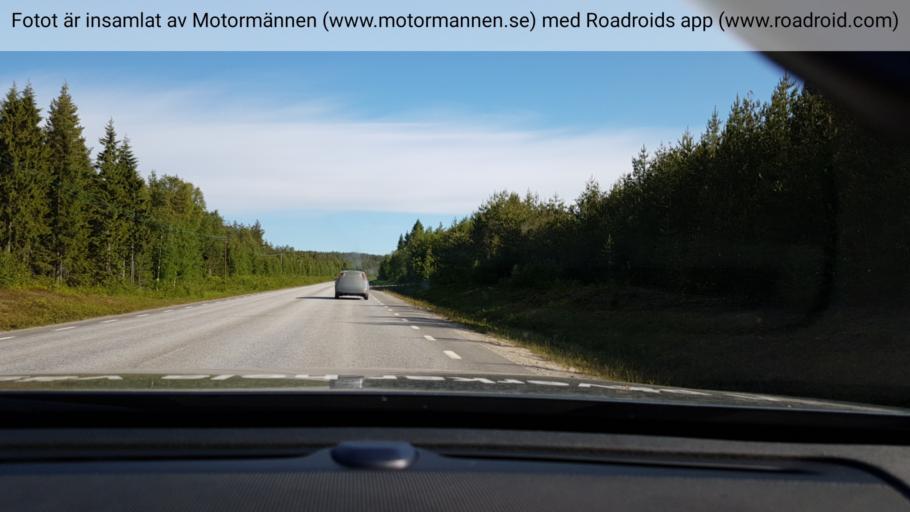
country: SE
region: Vaesterbotten
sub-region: Vannas Kommun
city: Vaennaes
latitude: 64.0213
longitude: 19.6926
